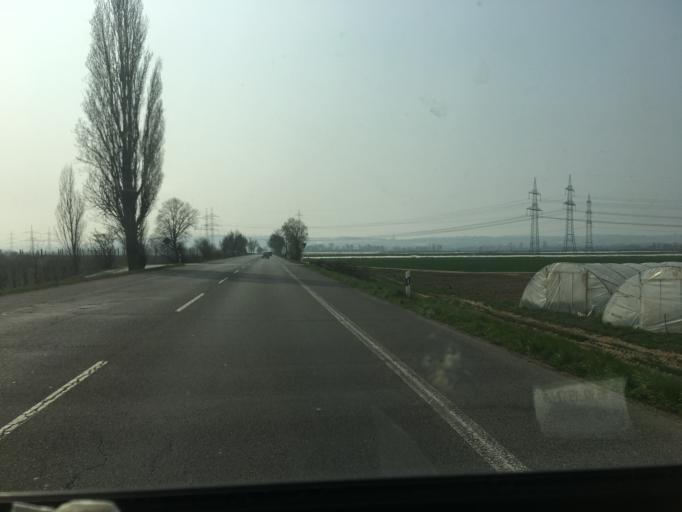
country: DE
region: North Rhine-Westphalia
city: Bornheim
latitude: 50.7872
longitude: 6.9922
